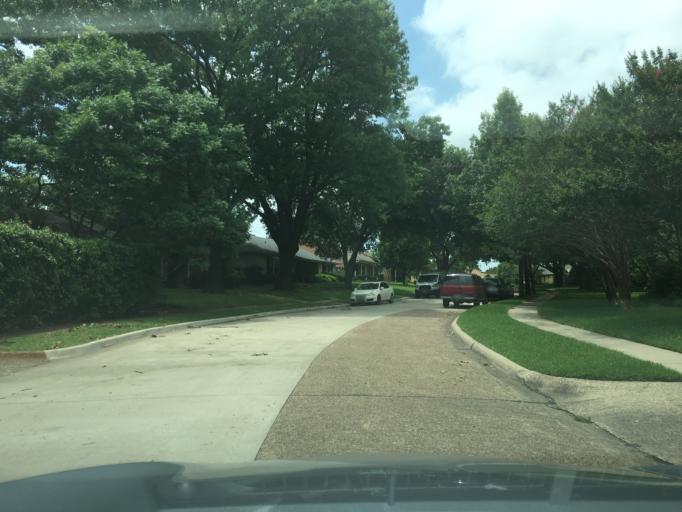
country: US
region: Texas
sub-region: Dallas County
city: Richardson
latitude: 32.9498
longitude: -96.7541
